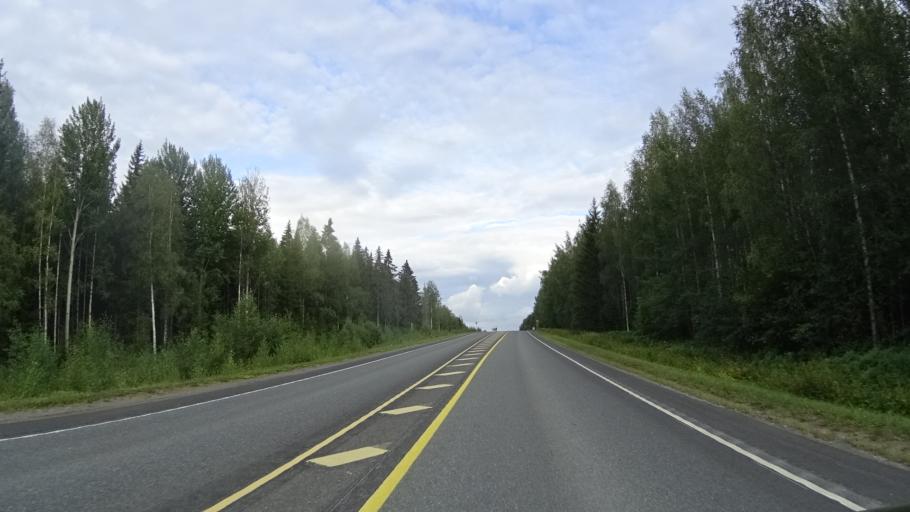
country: FI
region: Haeme
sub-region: Haemeenlinna
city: Parola
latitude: 61.0260
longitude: 24.3017
